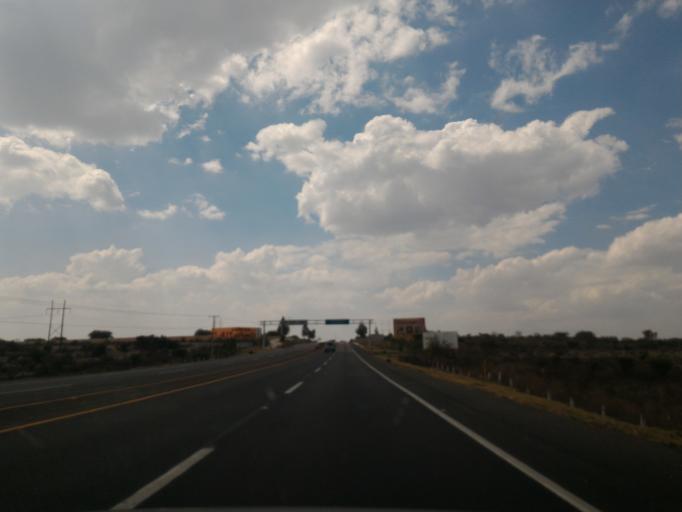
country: MX
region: Aguascalientes
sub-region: Aguascalientes
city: Penuelas (El Cienegal)
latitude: 21.6523
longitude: -102.2812
